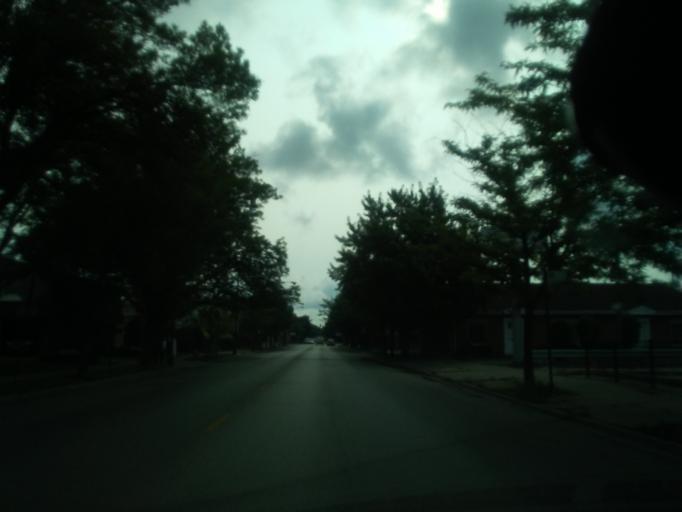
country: US
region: Illinois
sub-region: Cook County
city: Lincolnwood
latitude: 42.0120
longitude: -87.7018
